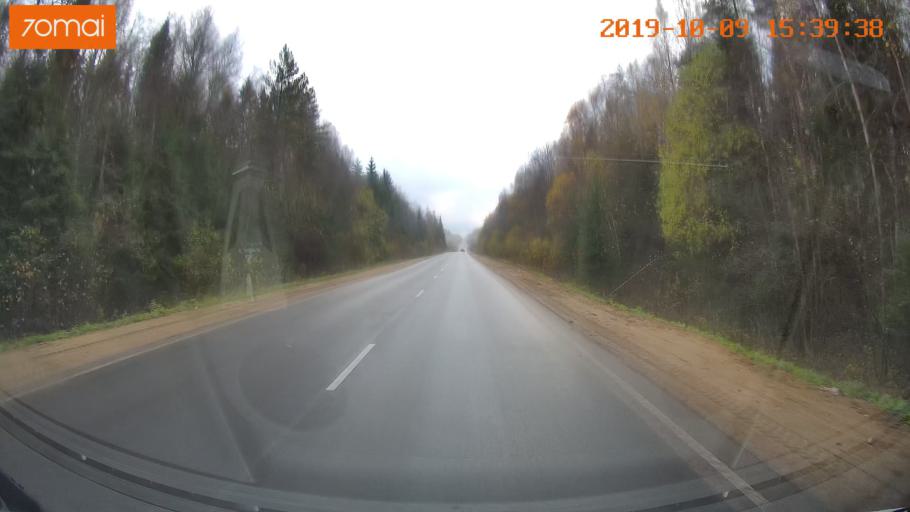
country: RU
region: Kostroma
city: Oktyabr'skiy
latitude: 57.8951
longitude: 41.1604
